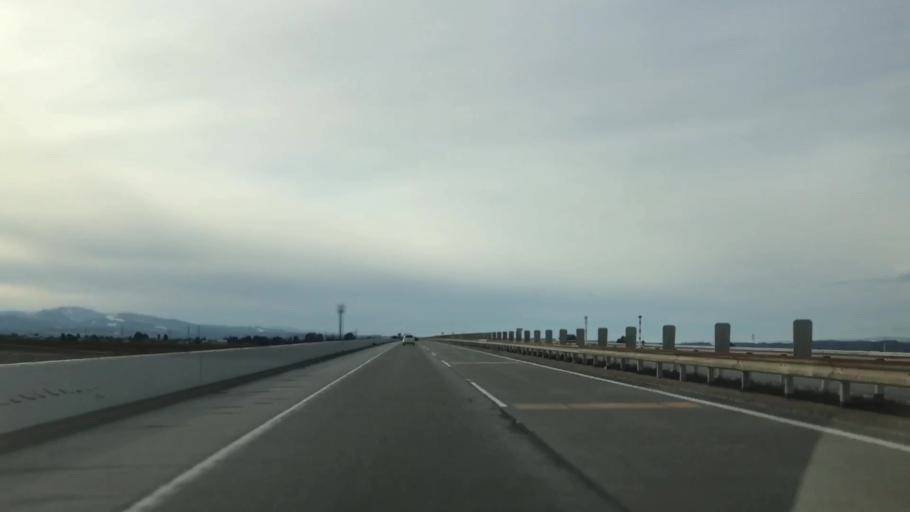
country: JP
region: Toyama
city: Toyama-shi
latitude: 36.6680
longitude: 137.2857
